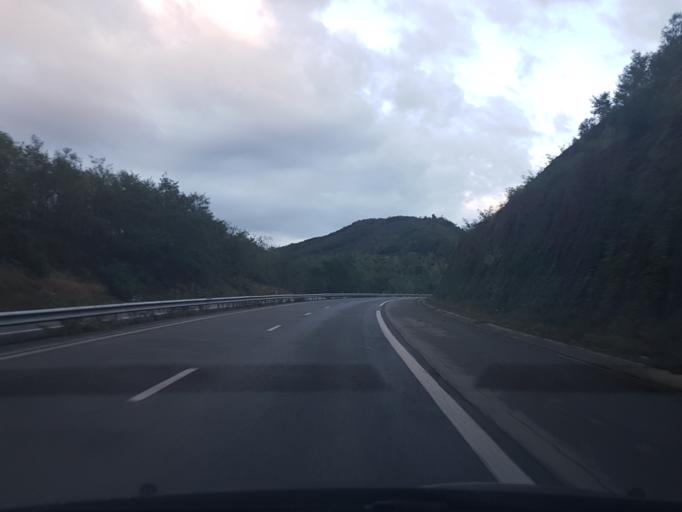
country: FR
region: Midi-Pyrenees
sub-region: Departement de l'Ariege
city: Foix
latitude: 42.9963
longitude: 1.6197
